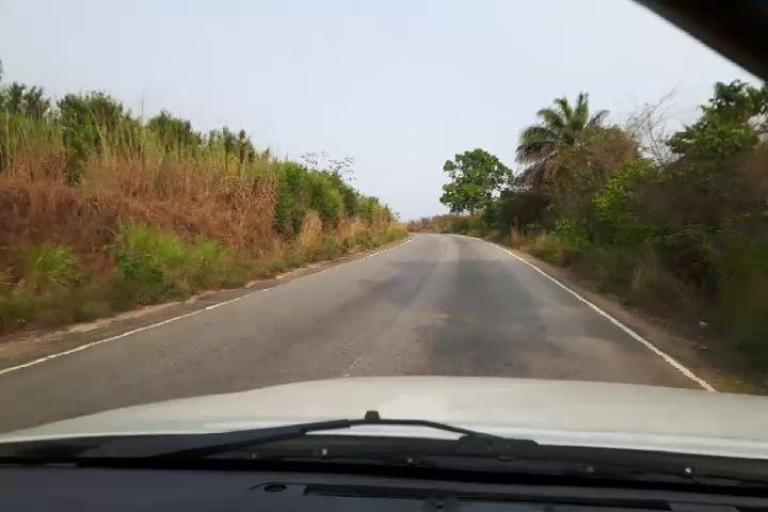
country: SL
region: Southern Province
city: Baoma
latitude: 7.9258
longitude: -11.5879
